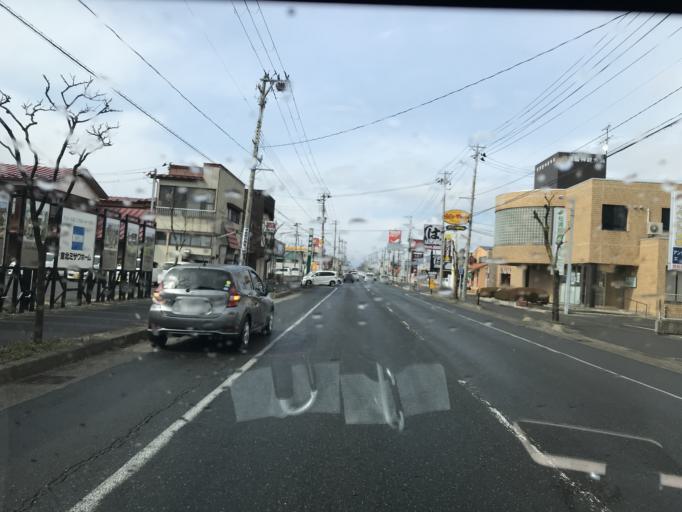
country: JP
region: Iwate
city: Kitakami
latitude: 39.3034
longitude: 141.1163
